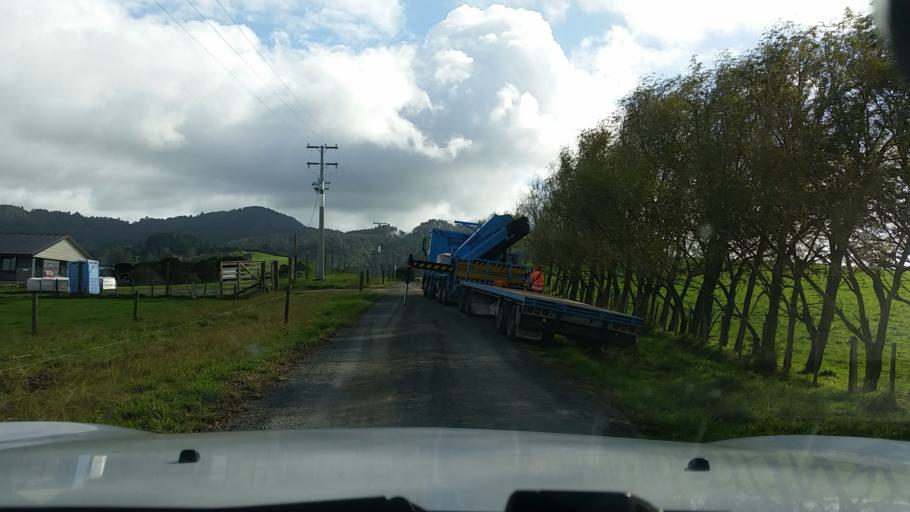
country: NZ
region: Waikato
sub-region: Hauraki District
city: Ngatea
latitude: -37.5000
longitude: 175.4043
